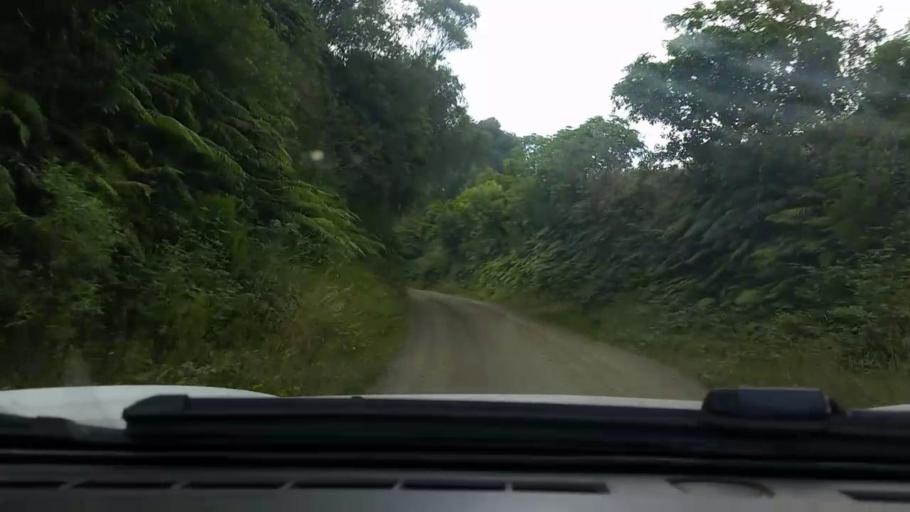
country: NZ
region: Bay of Plenty
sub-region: Kawerau District
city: Kawerau
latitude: -38.0086
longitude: 176.5984
